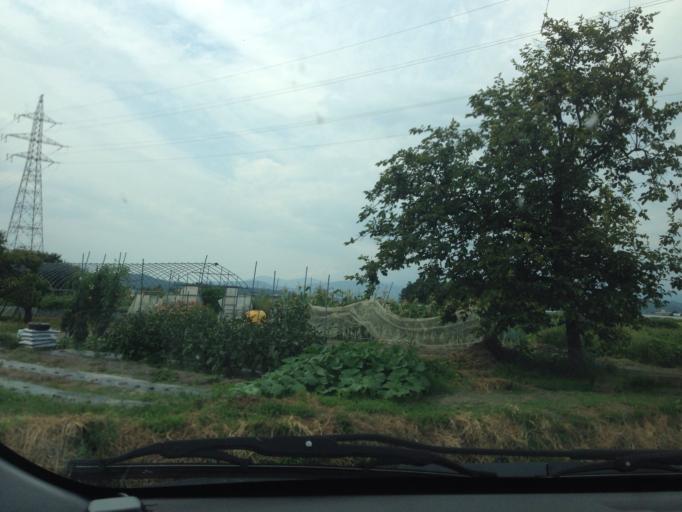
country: JP
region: Fukushima
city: Kitakata
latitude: 37.5749
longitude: 139.8386
